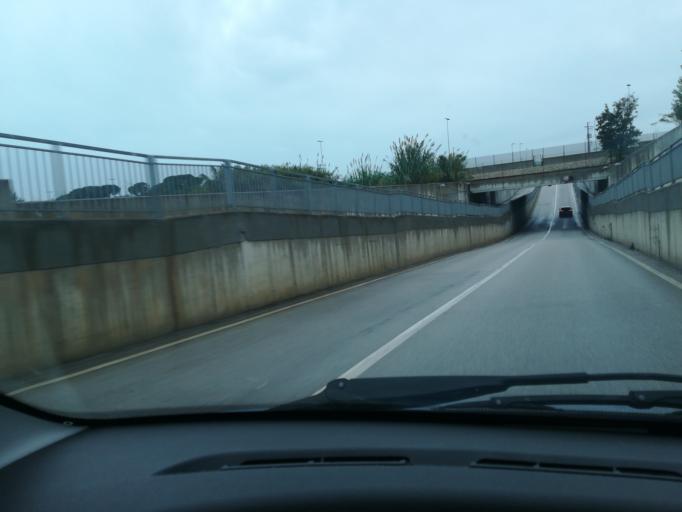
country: IT
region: The Marches
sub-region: Provincia di Macerata
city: Santa Maria Apparente
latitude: 43.2973
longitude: 13.7011
